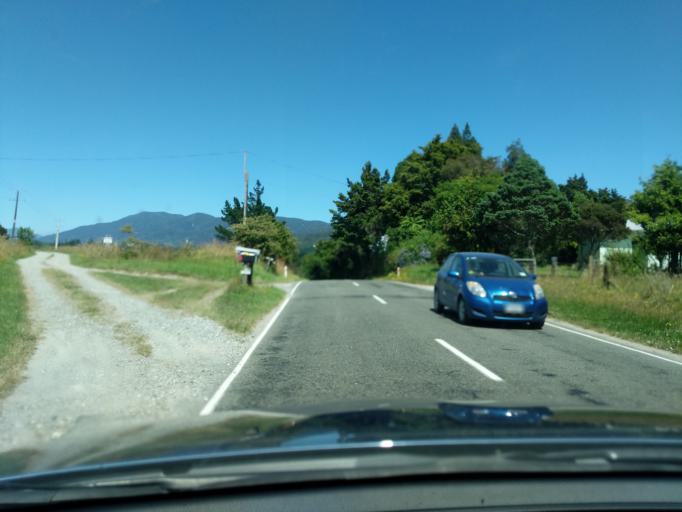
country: NZ
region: Tasman
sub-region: Tasman District
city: Takaka
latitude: -40.6951
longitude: 172.6347
